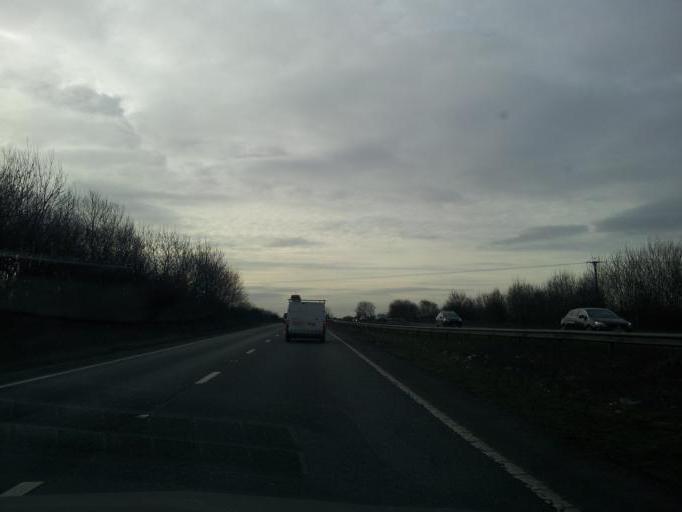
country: GB
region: England
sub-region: District of Rutland
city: Greetham
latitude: 52.7512
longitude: -0.6059
